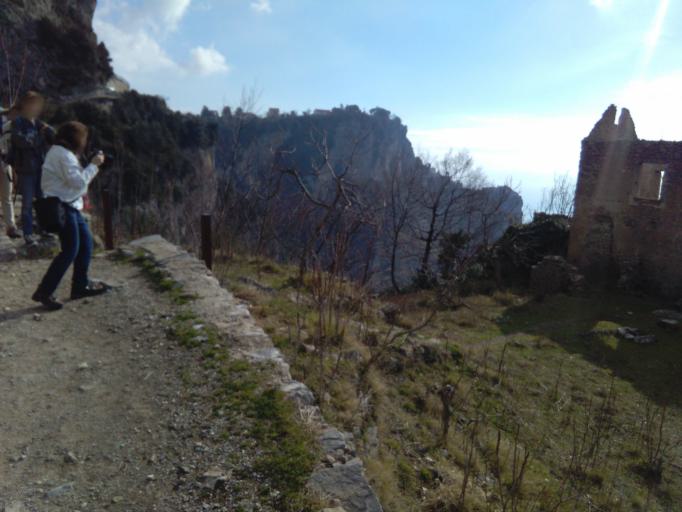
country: IT
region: Campania
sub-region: Provincia di Napoli
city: Agerola
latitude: 40.6249
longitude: 14.5326
